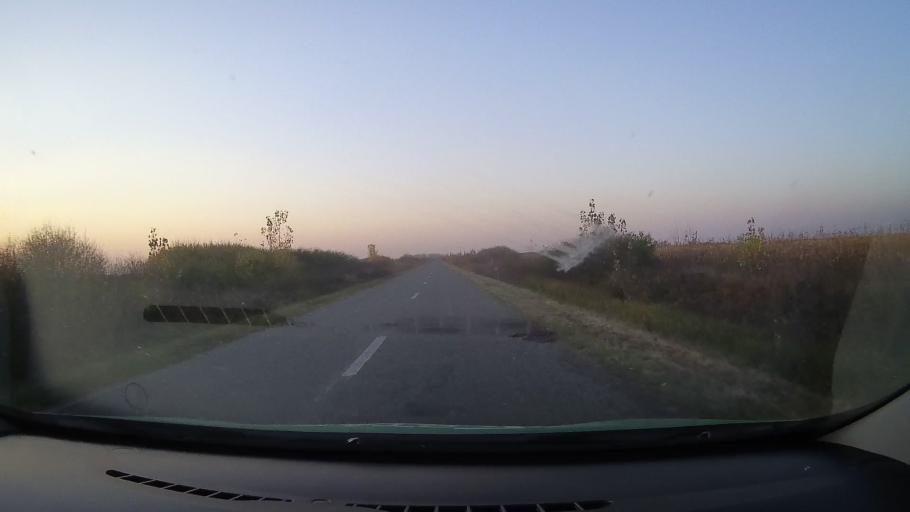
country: RO
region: Arad
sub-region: Comuna Zarand
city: Zarand
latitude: 46.3898
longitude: 21.6614
